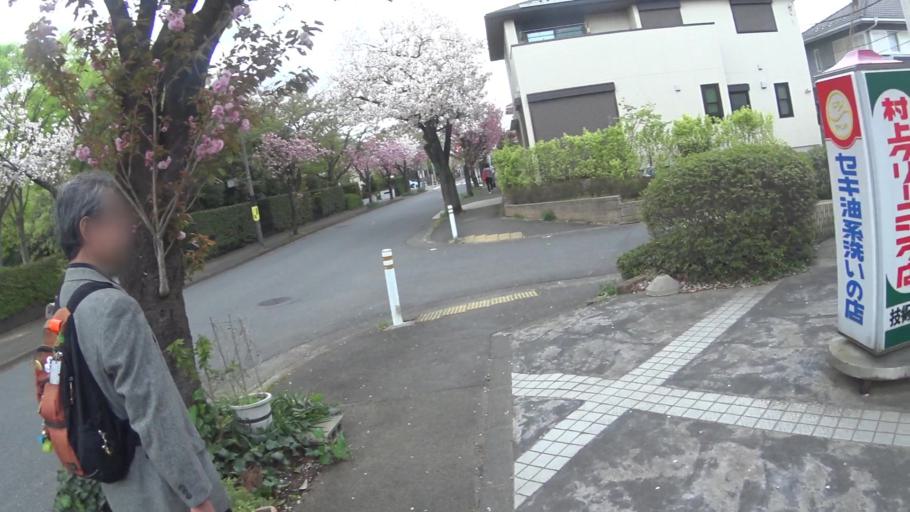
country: JP
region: Tokyo
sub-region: Machida-shi
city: Machida
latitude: 35.5744
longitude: 139.4890
